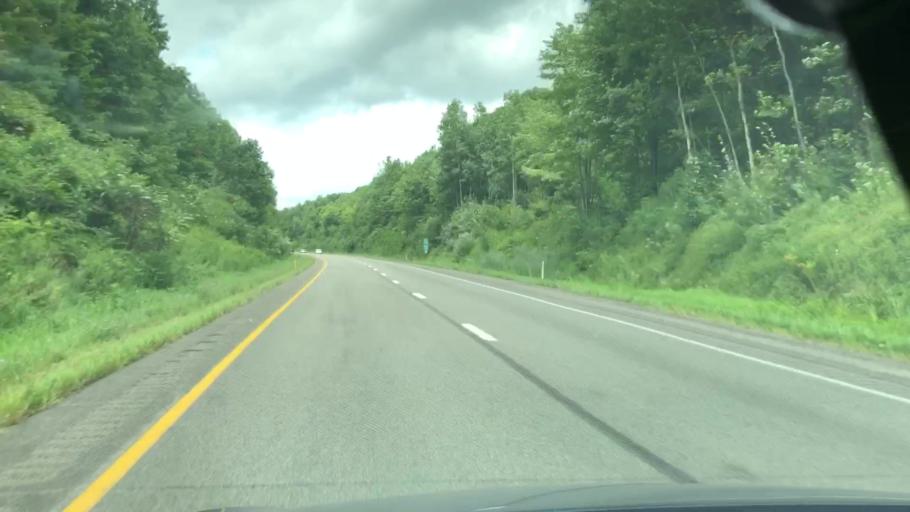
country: US
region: Pennsylvania
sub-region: Crawford County
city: Meadville
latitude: 41.7017
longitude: -80.1993
